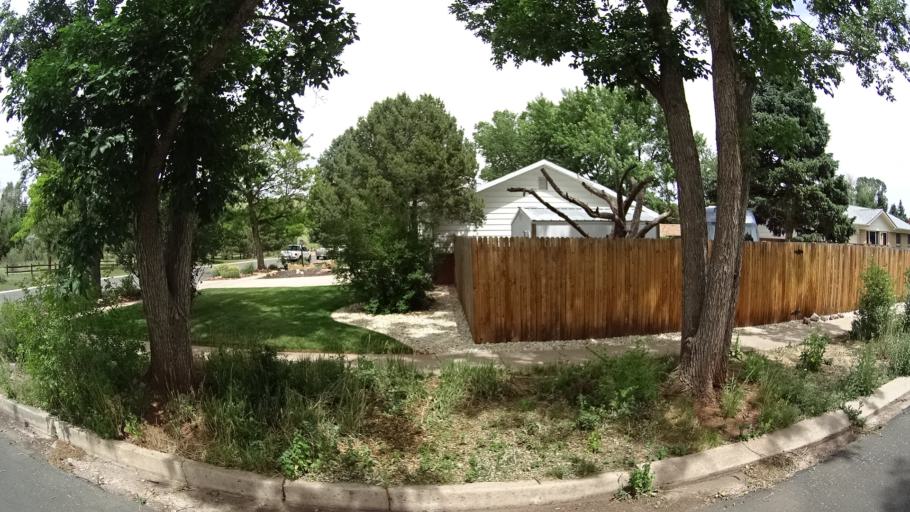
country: US
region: Colorado
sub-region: El Paso County
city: Manitou Springs
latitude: 38.8710
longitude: -104.8725
